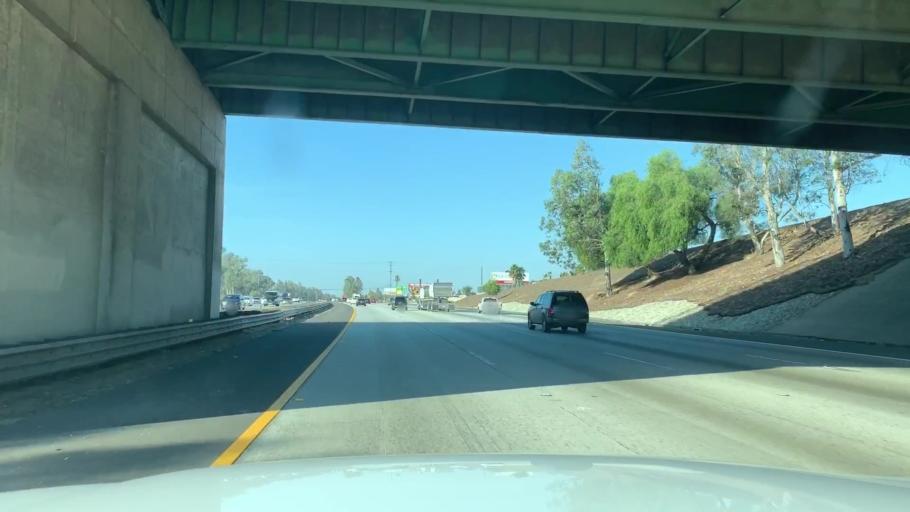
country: US
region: California
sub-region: San Bernardino County
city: Bloomington
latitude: 34.0686
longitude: -117.3960
